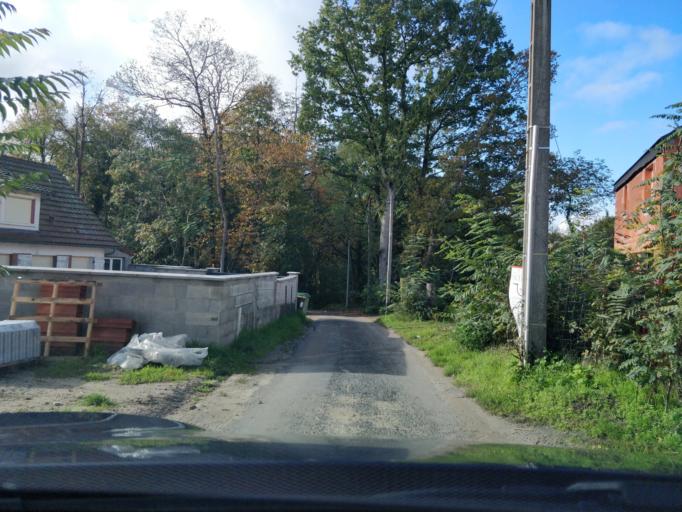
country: FR
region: Ile-de-France
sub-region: Departement de l'Essonne
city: Briis-sous-Forges
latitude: 48.6263
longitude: 2.1327
